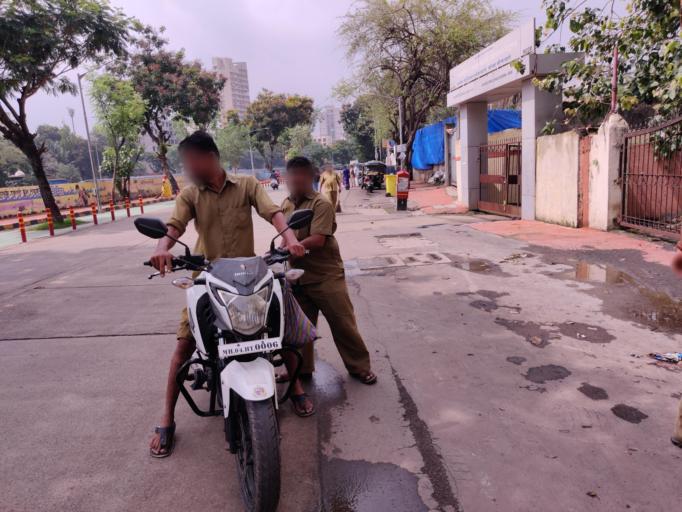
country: IN
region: Maharashtra
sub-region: Mumbai Suburban
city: Borivli
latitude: 19.2564
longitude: 72.8559
